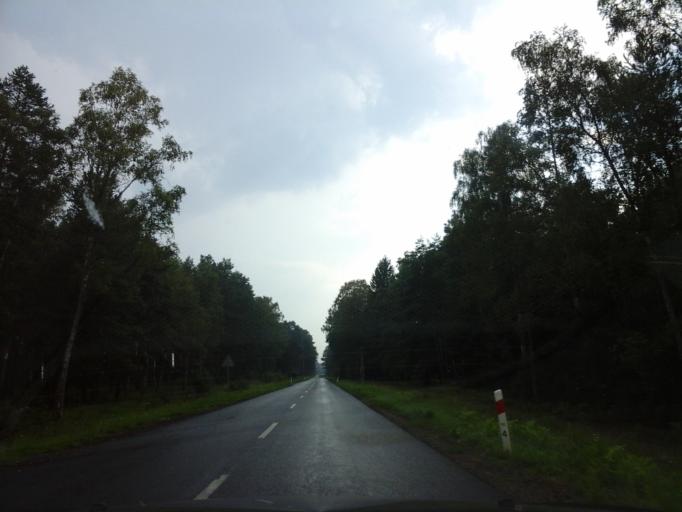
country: PL
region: Lubusz
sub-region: Powiat strzelecko-drezdenecki
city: Drezdenko
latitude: 52.7202
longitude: 15.8538
